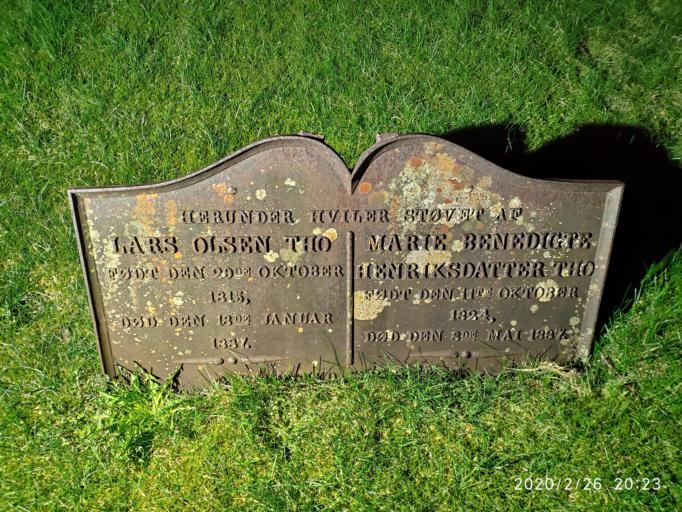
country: NO
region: Hordaland
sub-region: Tysnes
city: Uggdal
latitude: 60.0086
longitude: 5.4981
